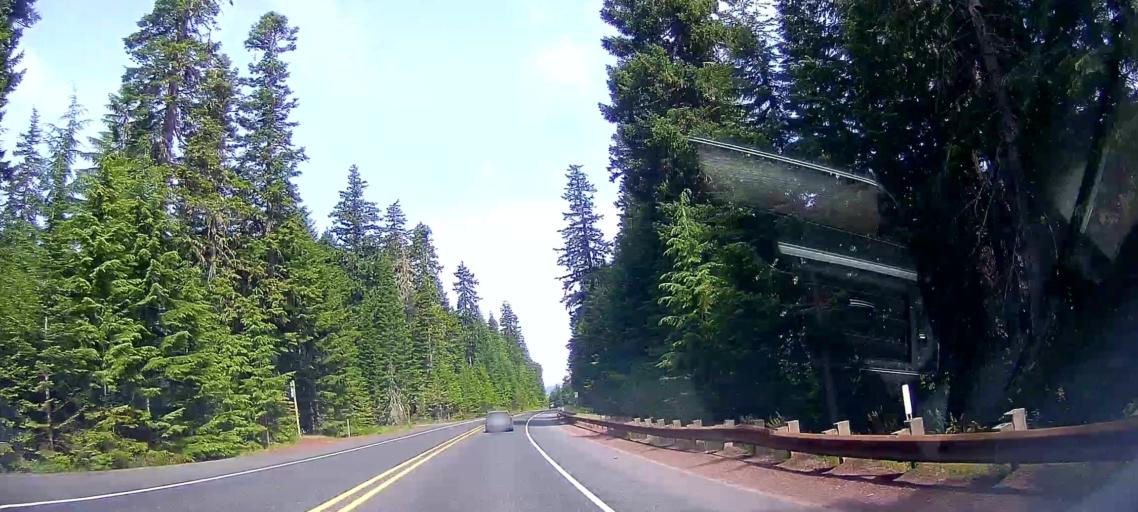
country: US
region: Oregon
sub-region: Clackamas County
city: Mount Hood Village
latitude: 45.1350
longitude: -121.6157
